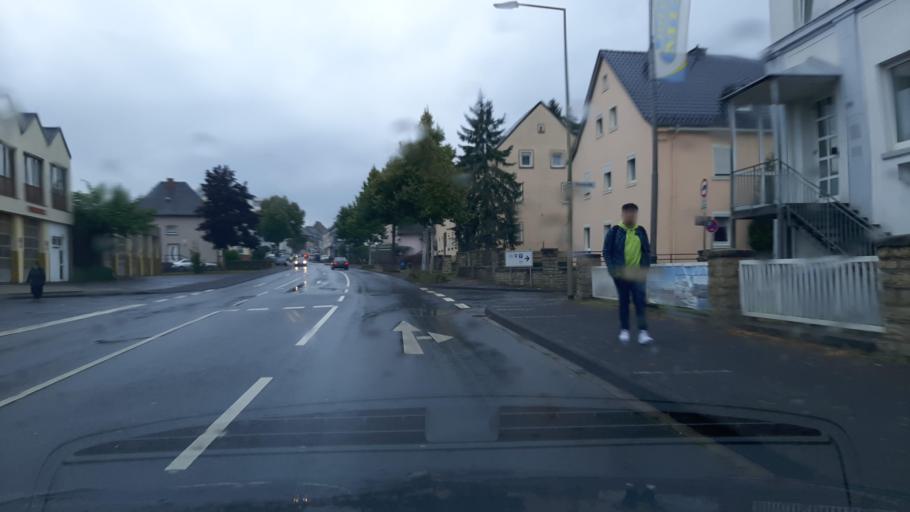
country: DE
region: Rheinland-Pfalz
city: Bitburg
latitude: 49.9675
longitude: 6.5275
